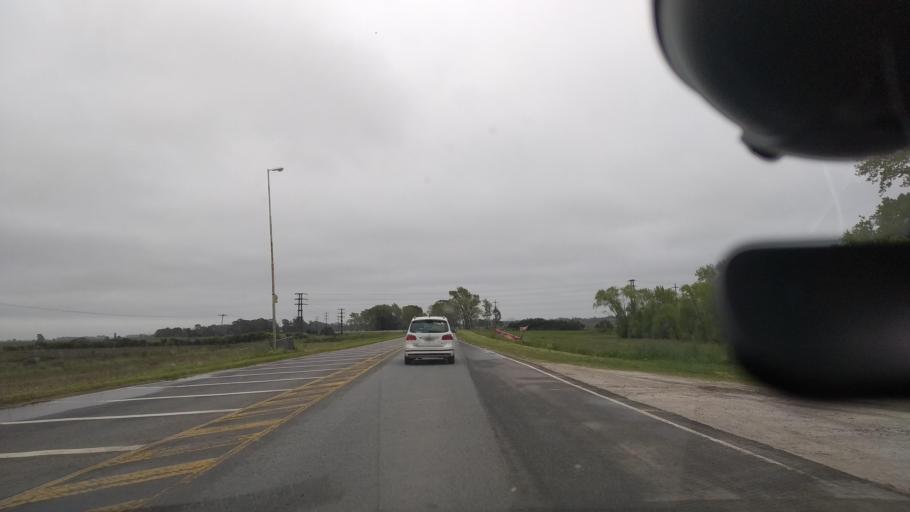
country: AR
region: Buenos Aires
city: Veronica
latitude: -35.3824
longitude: -57.3665
